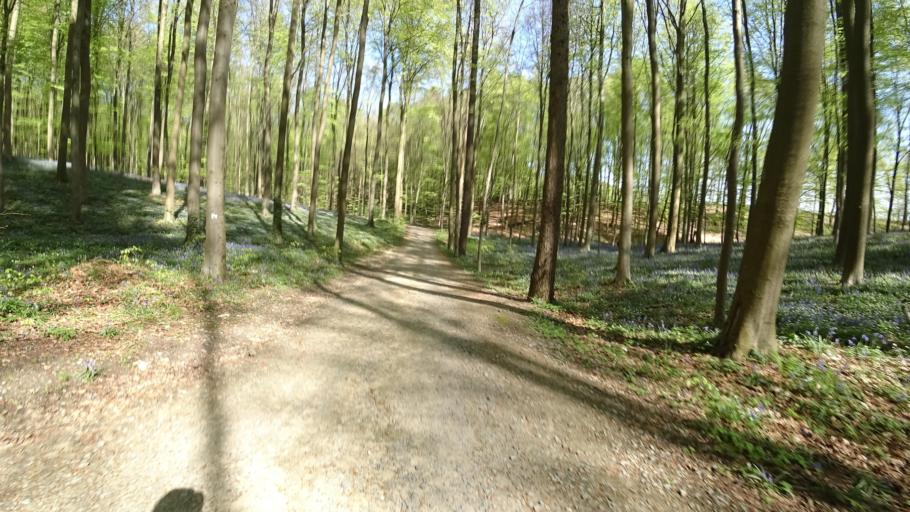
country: BE
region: Wallonia
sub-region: Province du Brabant Wallon
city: Braine-le-Chateau
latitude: 50.7029
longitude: 4.3097
